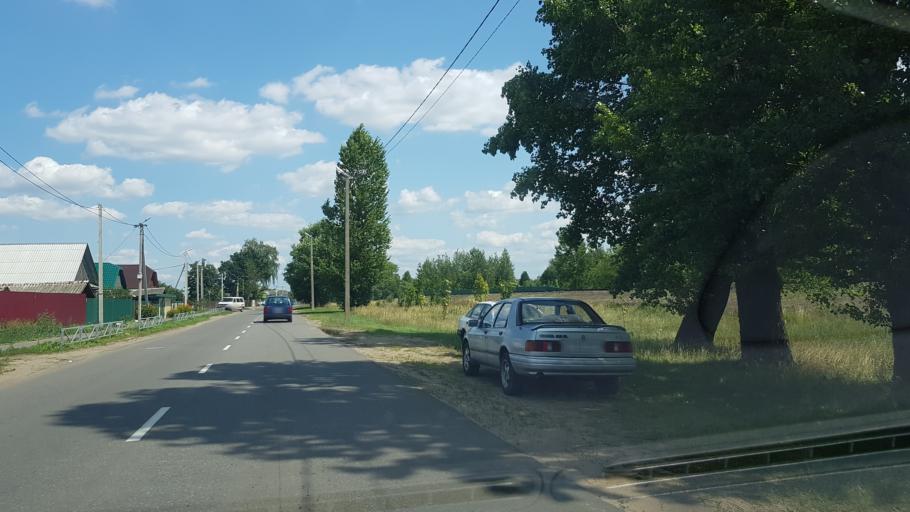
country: BY
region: Mogilev
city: Babruysk
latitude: 53.1125
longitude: 29.2053
